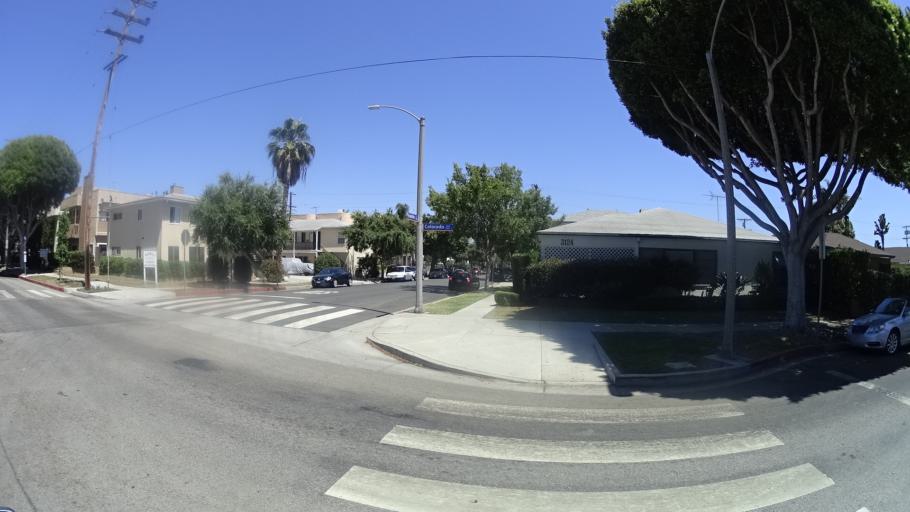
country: US
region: California
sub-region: Los Angeles County
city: Santa Monica
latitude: 34.0351
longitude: -118.4656
